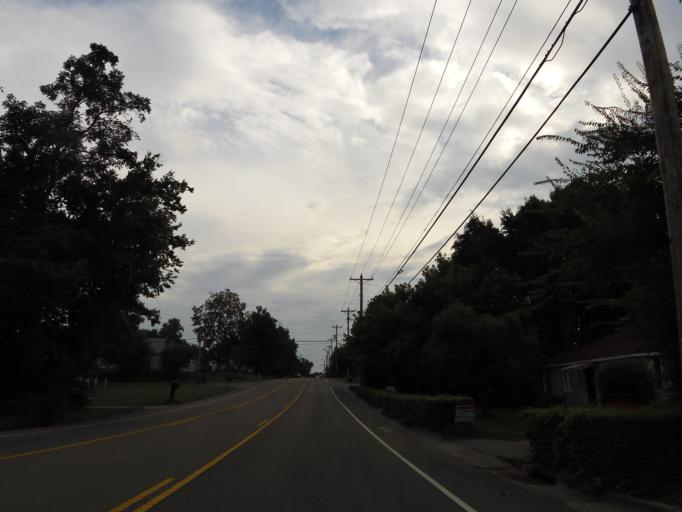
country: US
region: Tennessee
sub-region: Blount County
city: Alcoa
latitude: 35.7742
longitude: -83.9632
